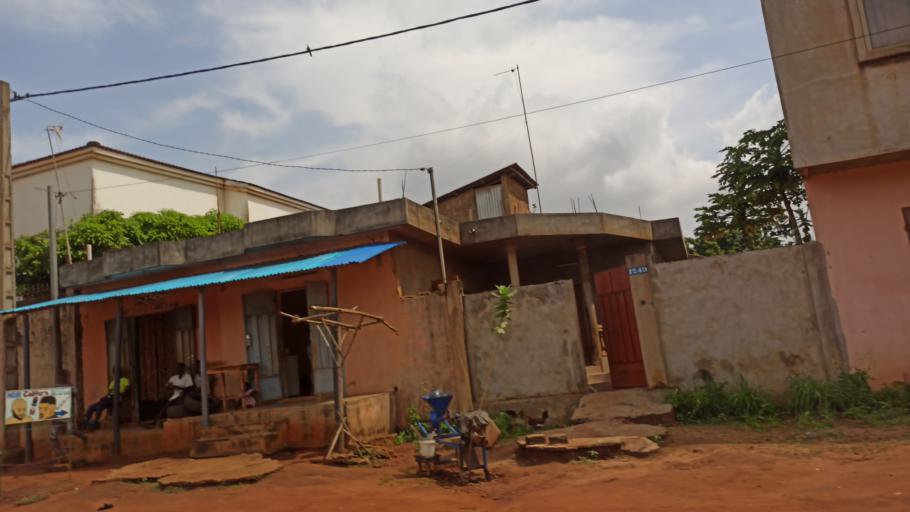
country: BJ
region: Queme
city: Porto-Novo
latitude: 6.4848
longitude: 2.5908
